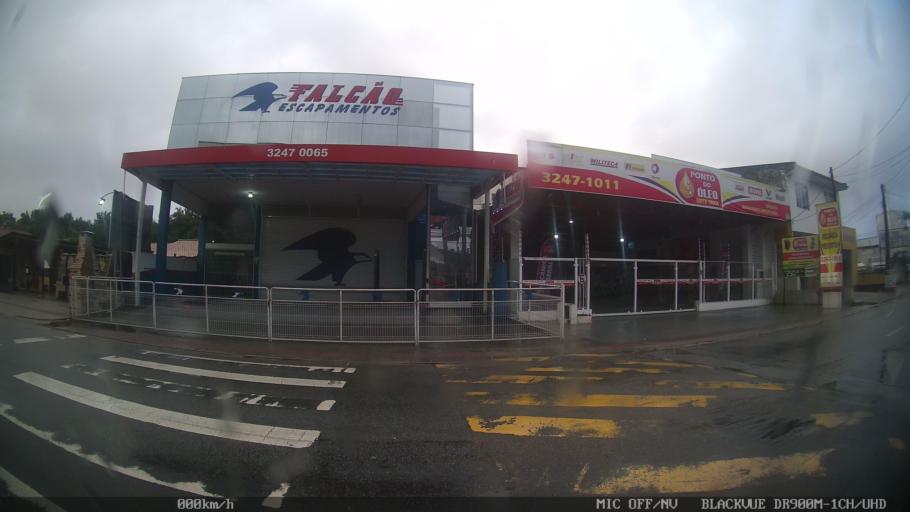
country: BR
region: Santa Catarina
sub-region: Sao Jose
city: Campinas
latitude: -27.6038
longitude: -48.6214
